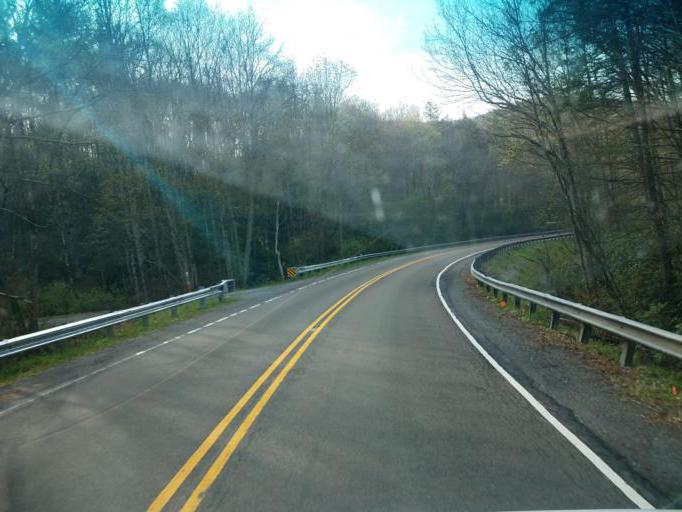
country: US
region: Virginia
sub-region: Smyth County
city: Atkins
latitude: 36.8097
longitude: -81.4048
